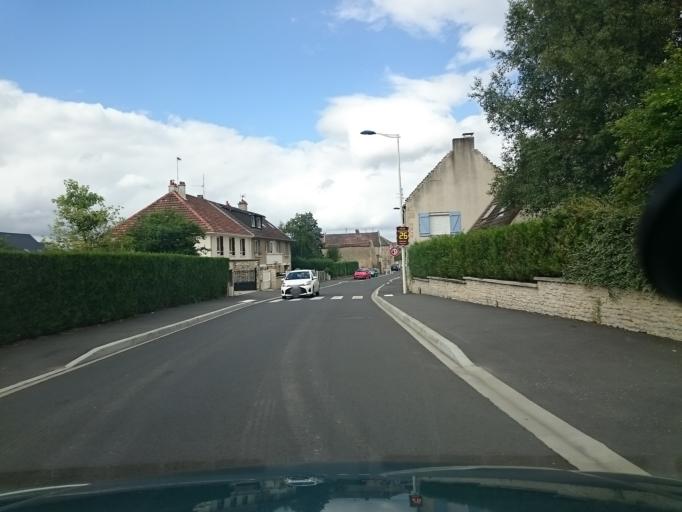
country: FR
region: Lower Normandy
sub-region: Departement du Calvados
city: Ifs
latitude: 49.1412
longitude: -0.3487
